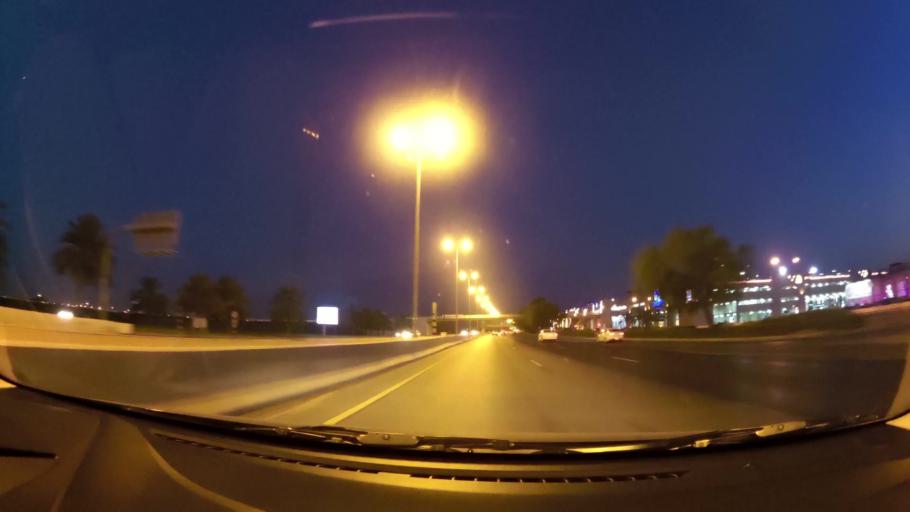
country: OM
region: Muhafazat Masqat
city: As Sib al Jadidah
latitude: 23.6034
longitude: 58.2492
